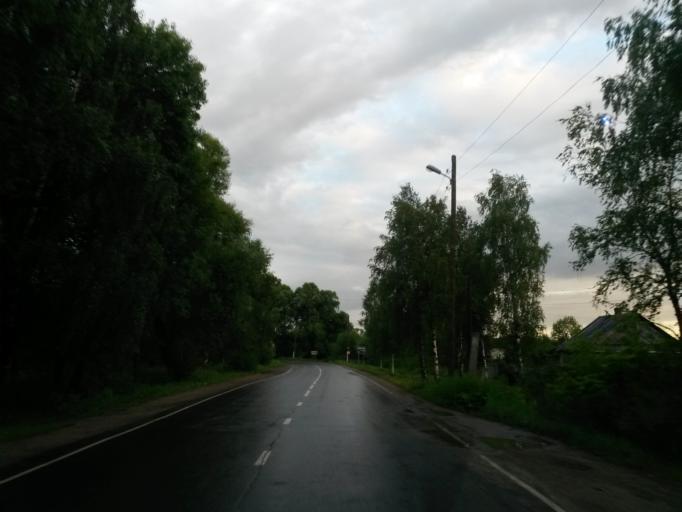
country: RU
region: Jaroslavl
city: Tutayev
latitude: 57.8934
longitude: 39.5286
